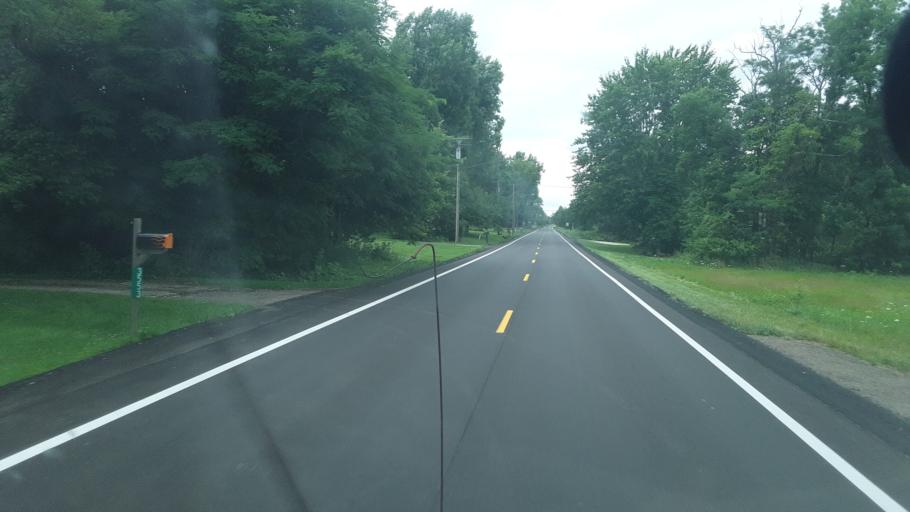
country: US
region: Ohio
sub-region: Trumbull County
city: Cortland
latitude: 41.3136
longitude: -80.6557
